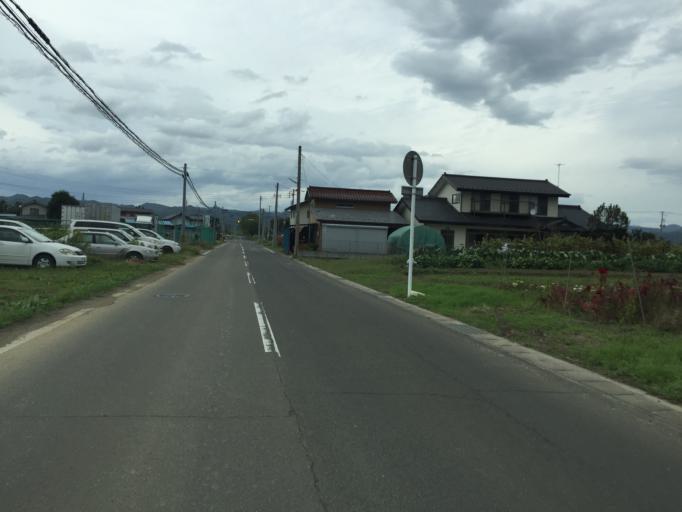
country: JP
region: Fukushima
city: Yanagawamachi-saiwaicho
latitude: 37.8553
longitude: 140.5888
